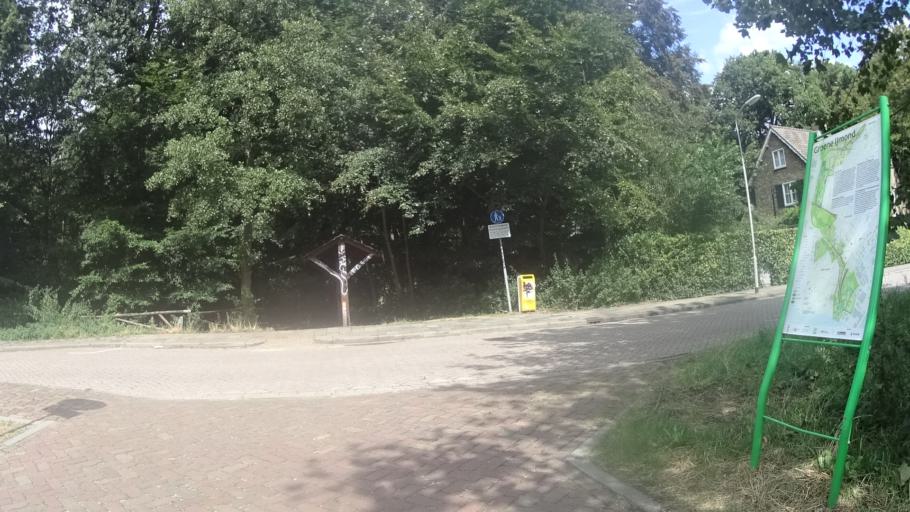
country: NL
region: North Holland
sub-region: Gemeente Beverwijk
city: Beverwijk
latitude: 52.4824
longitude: 4.6414
